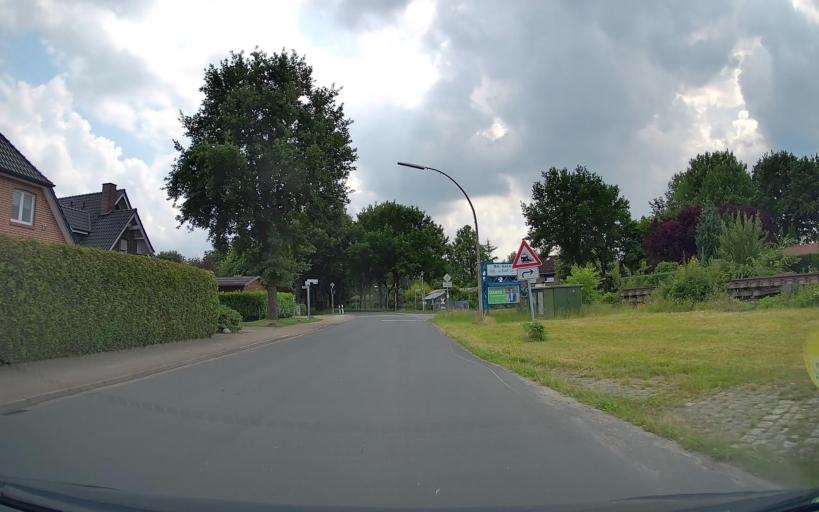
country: DE
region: Lower Saxony
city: Bosel
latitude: 52.9999
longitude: 7.9476
